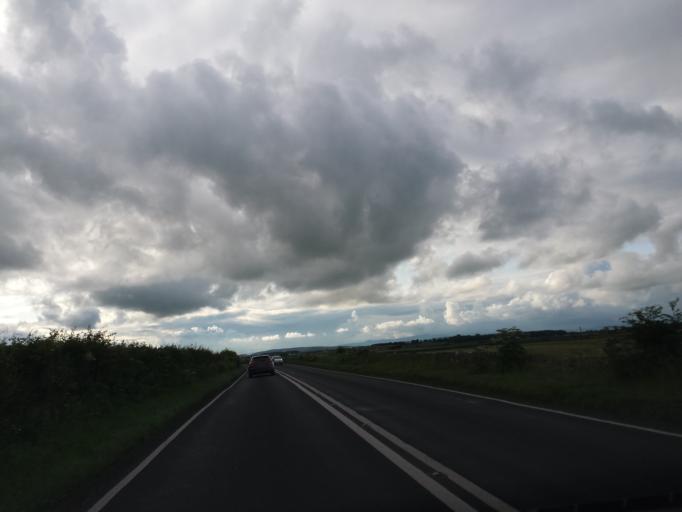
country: GB
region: Scotland
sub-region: Fife
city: Strathkinness
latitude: 56.3545
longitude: -2.8552
